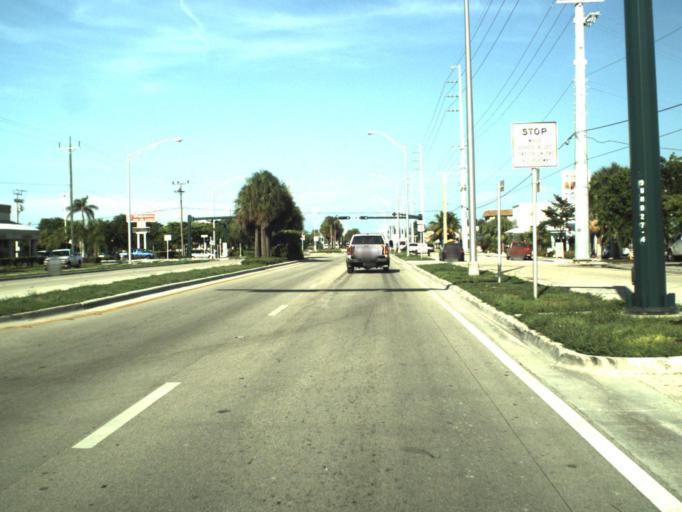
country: US
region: Florida
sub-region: Monroe County
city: Marathon
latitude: 24.7284
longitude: -81.0391
